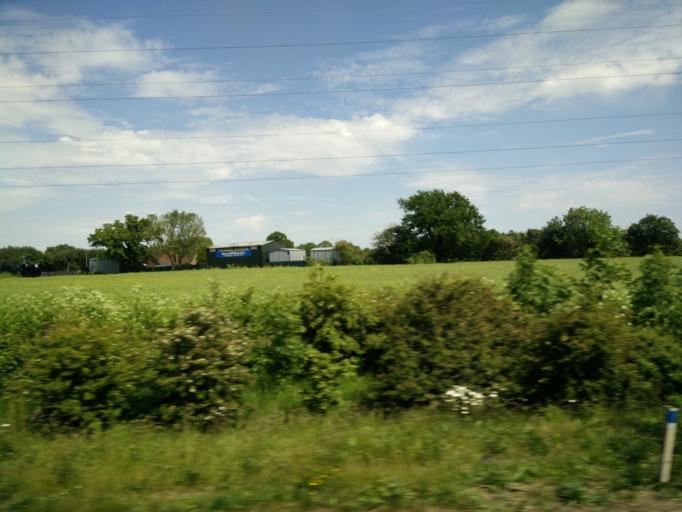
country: GB
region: England
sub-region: Hertfordshire
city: Flamstead
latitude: 51.8329
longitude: -0.4190
